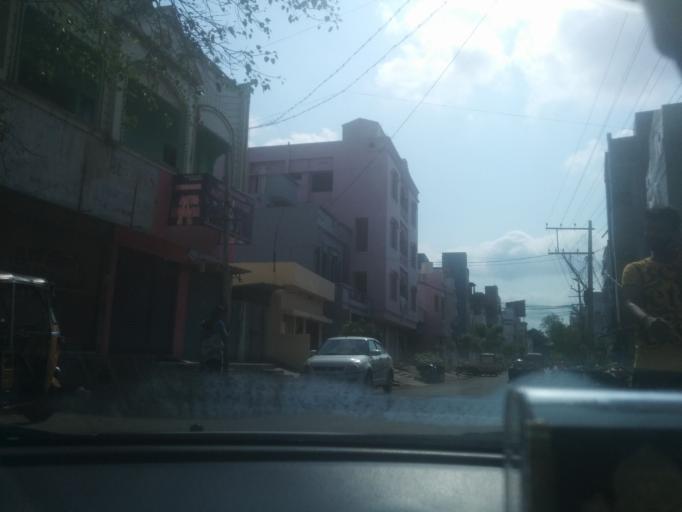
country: IN
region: Andhra Pradesh
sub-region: East Godavari
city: Rajahmundry
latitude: 17.0130
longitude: 81.7763
